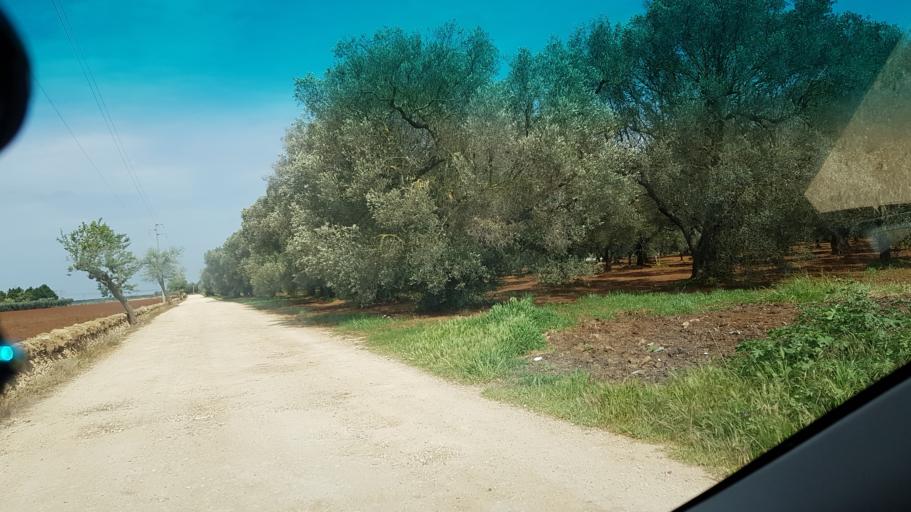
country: IT
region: Apulia
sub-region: Provincia di Brindisi
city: Mesagne
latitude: 40.5994
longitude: 17.8548
